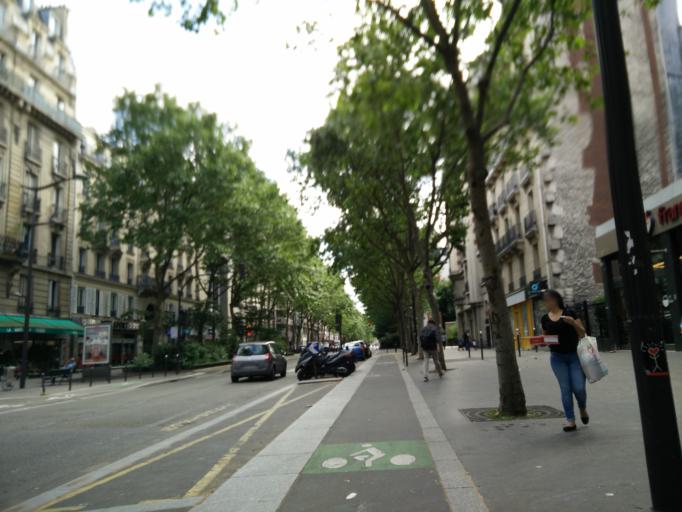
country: FR
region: Ile-de-France
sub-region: Departement de Seine-Saint-Denis
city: Le Pre-Saint-Gervais
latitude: 48.8845
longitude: 2.3761
